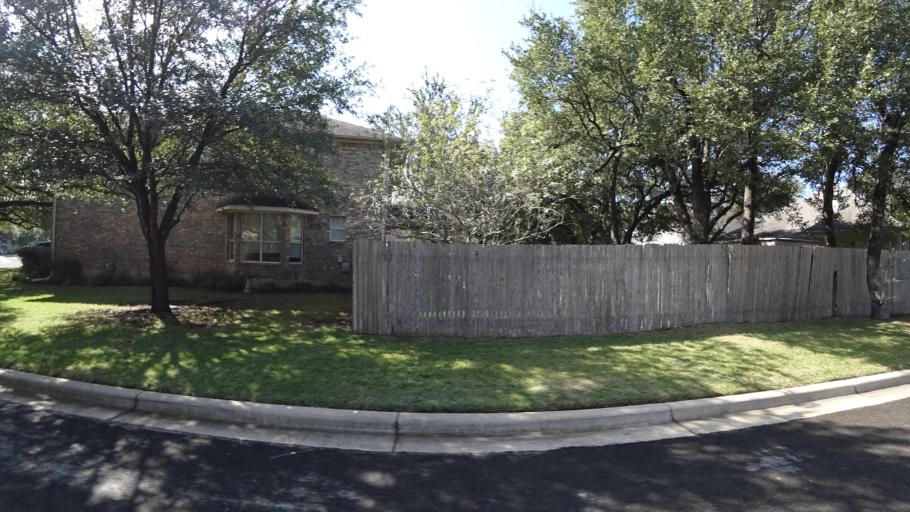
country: US
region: Texas
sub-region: Travis County
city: Shady Hollow
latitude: 30.2065
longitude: -97.8737
